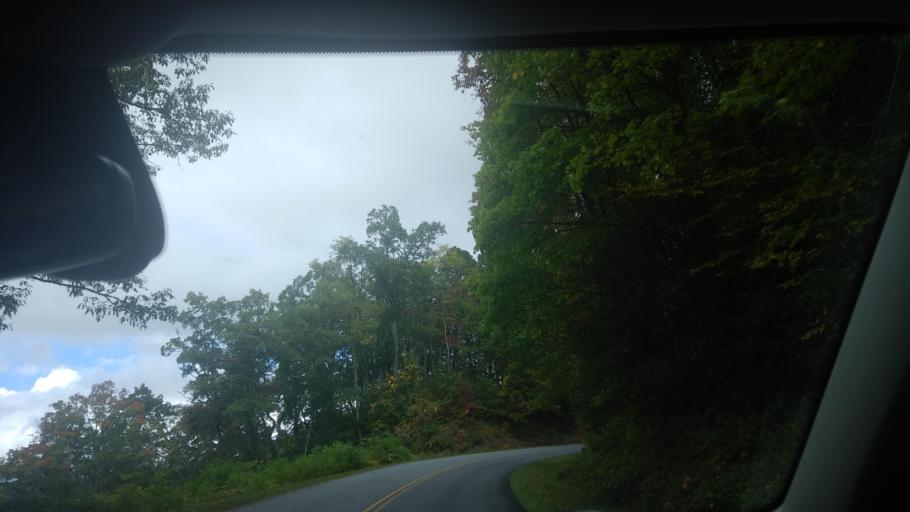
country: US
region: North Carolina
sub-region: Swain County
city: Cherokee
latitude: 35.5159
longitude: -83.2561
